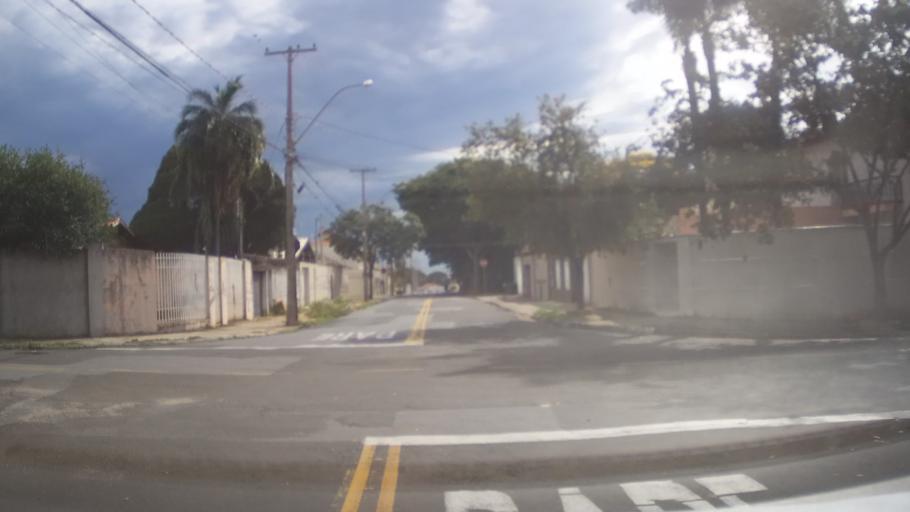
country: BR
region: Sao Paulo
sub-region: Campinas
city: Campinas
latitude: -22.8874
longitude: -47.1054
